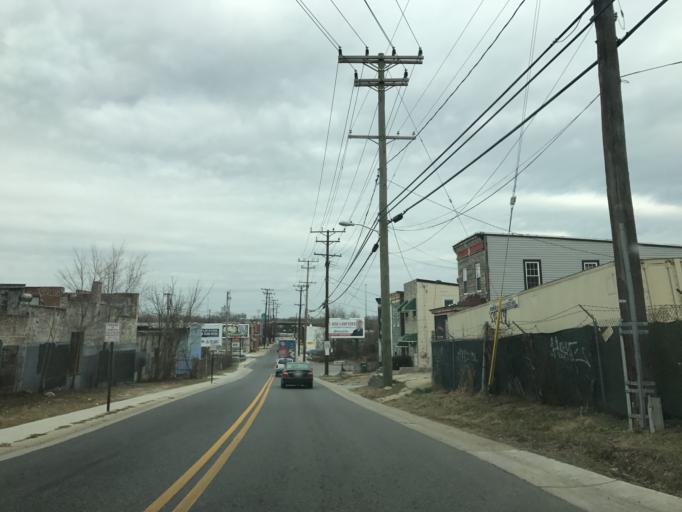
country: US
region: Maryland
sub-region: Baltimore County
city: Lansdowne
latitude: 39.2674
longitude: -76.6455
